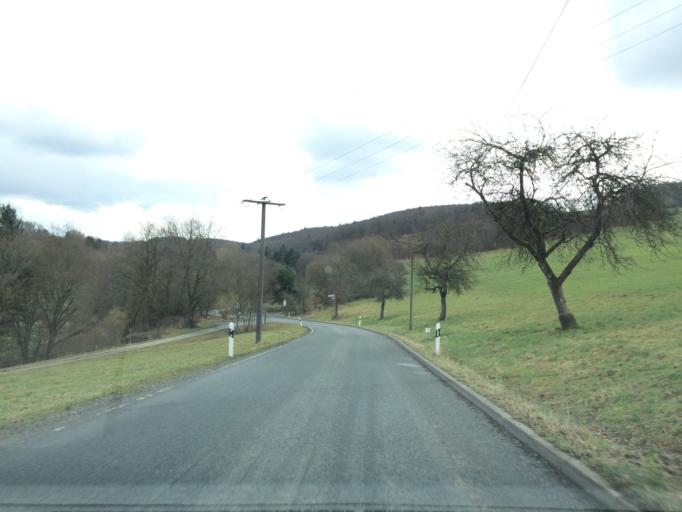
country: DE
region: Hesse
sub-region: Regierungsbezirk Darmstadt
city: Gravenwiesbach
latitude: 50.3831
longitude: 8.4068
